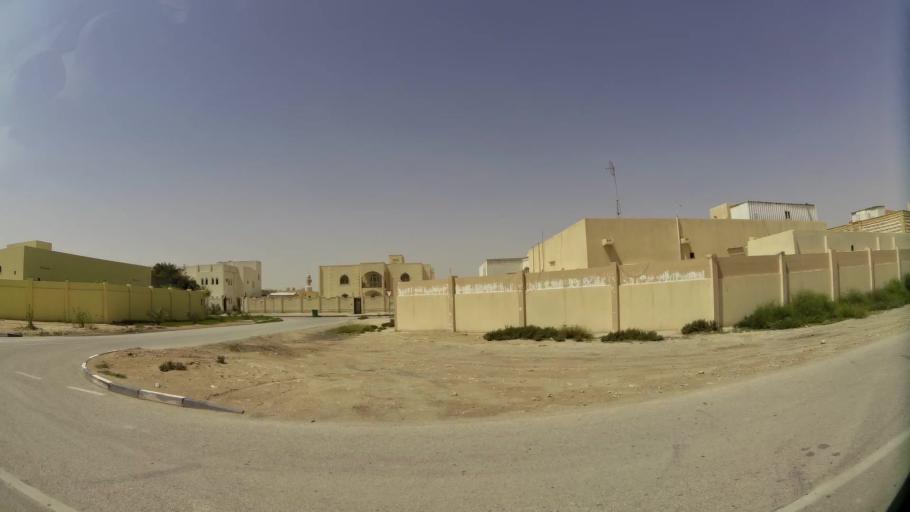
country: QA
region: Baladiyat Umm Salal
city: Umm Salal Muhammad
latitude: 25.3769
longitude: 51.4756
